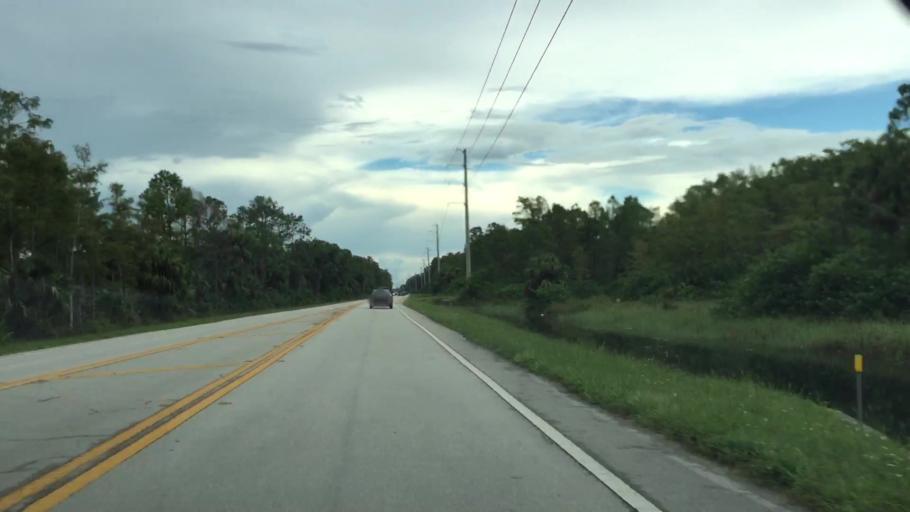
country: US
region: Florida
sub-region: Collier County
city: Orangetree
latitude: 26.3294
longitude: -81.5950
